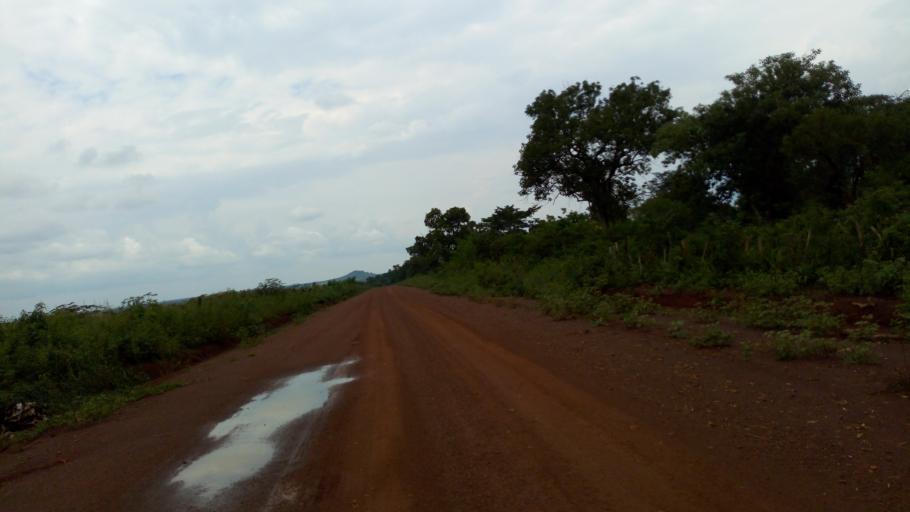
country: UG
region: Western Region
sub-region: Masindi District
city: Masindi
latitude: 1.5456
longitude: 31.7487
